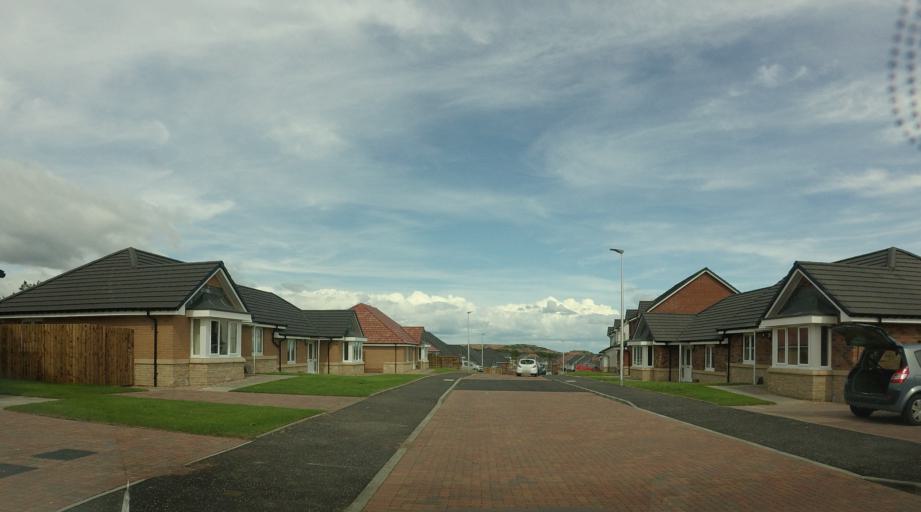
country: GB
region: Scotland
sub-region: West Lothian
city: Broxburn
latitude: 55.9367
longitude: -3.5015
